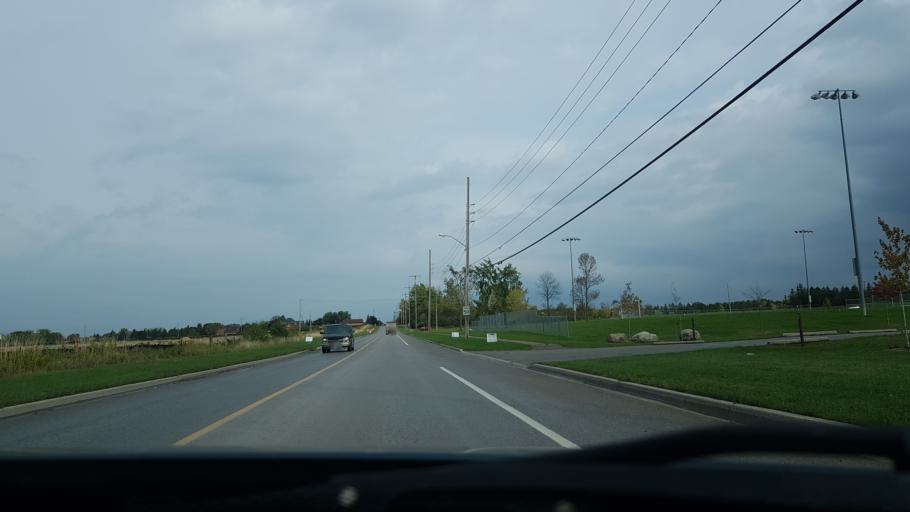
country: CA
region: Ontario
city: Omemee
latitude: 44.3547
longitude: -78.7652
